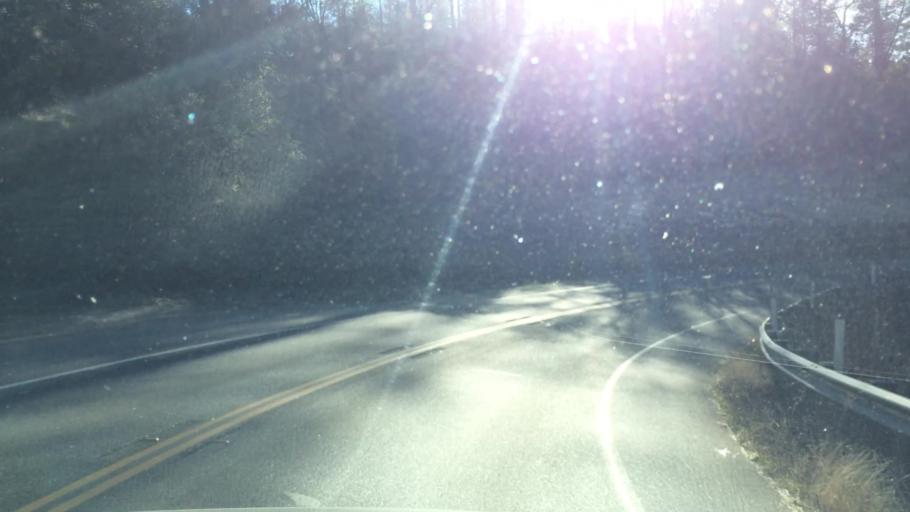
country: US
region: California
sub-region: Nevada County
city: Penn Valley
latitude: 39.2155
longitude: -121.1567
